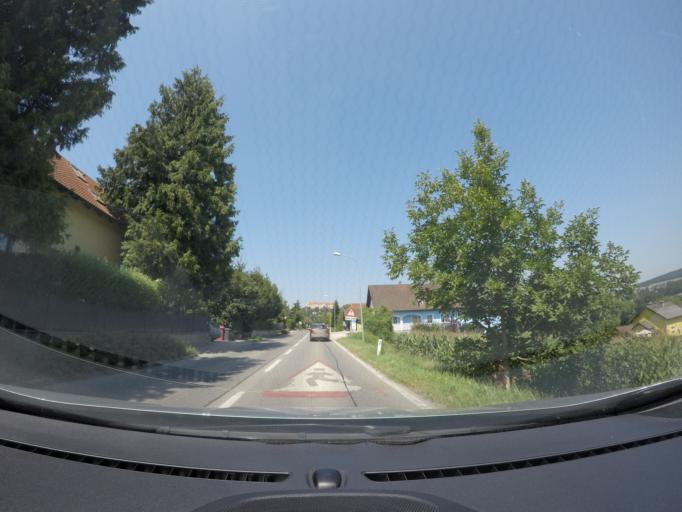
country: AT
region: Lower Austria
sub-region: Politischer Bezirk Sankt Polten
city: Maria-Anzbach
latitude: 48.1932
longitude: 15.9176
